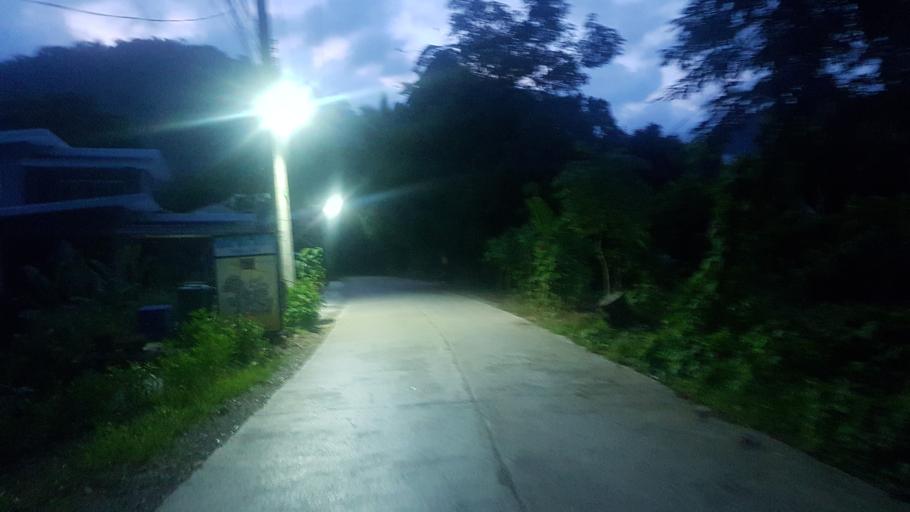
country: TH
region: Phangnga
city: Takua Pa
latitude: 8.9121
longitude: 98.5270
